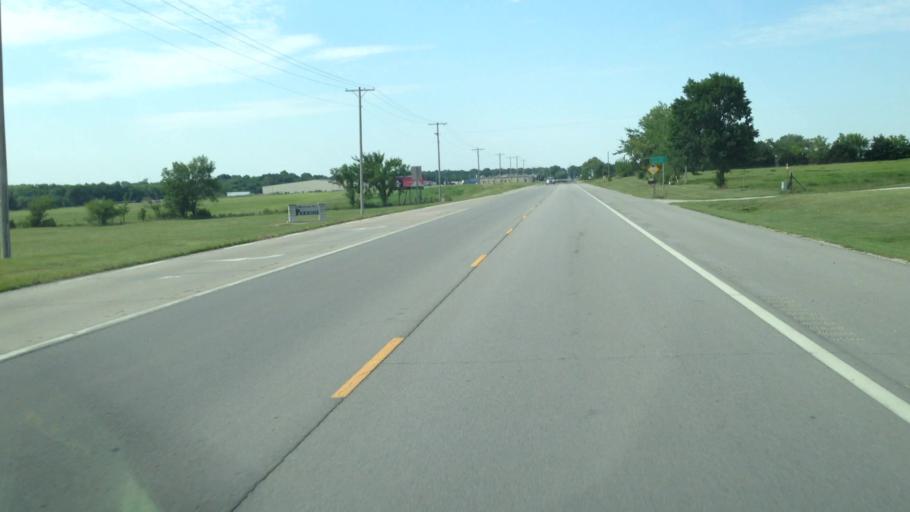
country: US
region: Kansas
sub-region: Labette County
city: Parsons
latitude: 37.3113
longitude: -95.2675
